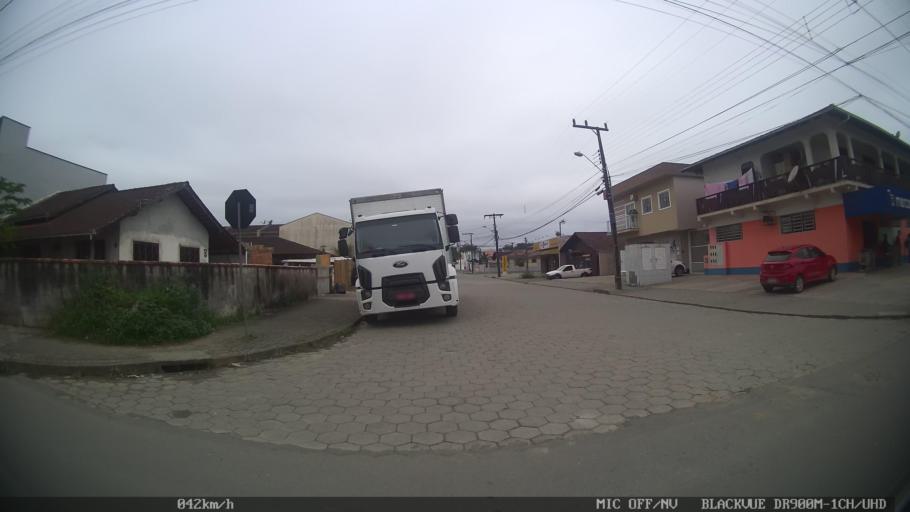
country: BR
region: Santa Catarina
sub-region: Joinville
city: Joinville
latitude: -26.2927
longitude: -48.9098
